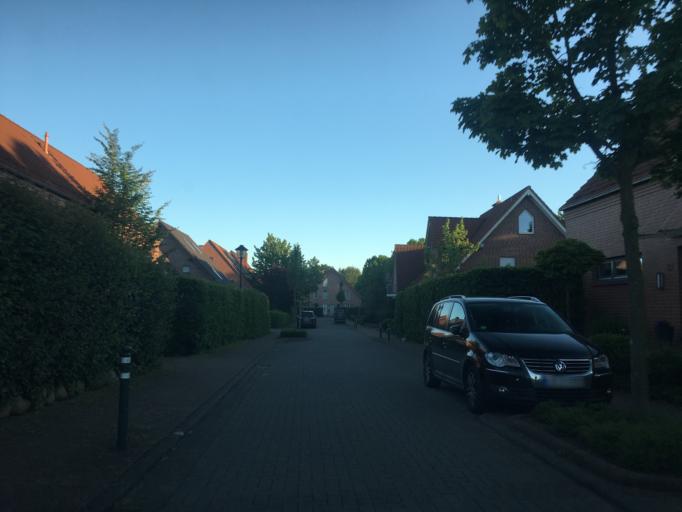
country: DE
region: North Rhine-Westphalia
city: Ludinghausen
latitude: 51.7632
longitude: 7.4573
